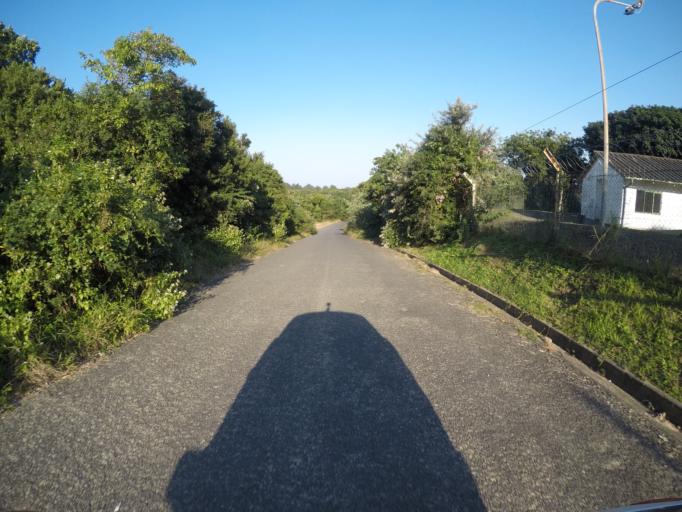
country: ZA
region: KwaZulu-Natal
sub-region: uThungulu District Municipality
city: Richards Bay
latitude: -28.7821
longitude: 32.0870
